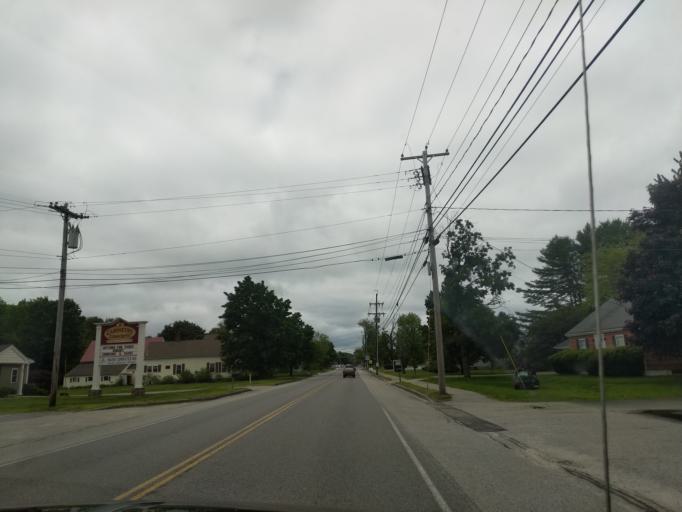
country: US
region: Maine
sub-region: Cumberland County
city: North Windham
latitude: 43.8352
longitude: -70.4337
